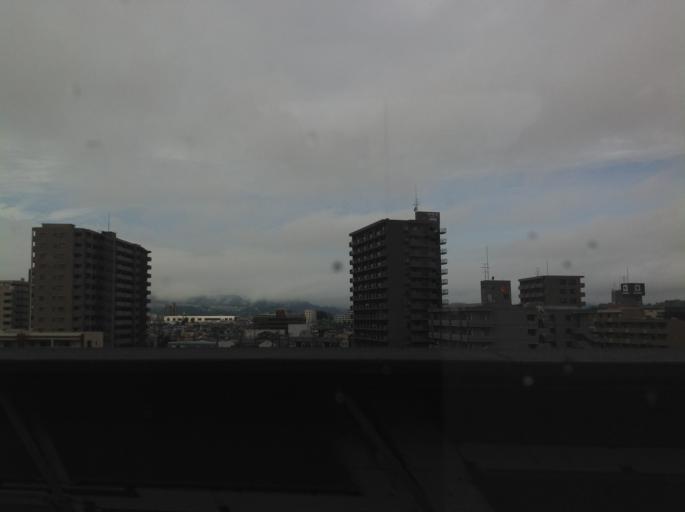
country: JP
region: Miyagi
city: Sendai
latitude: 38.2172
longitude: 140.8831
